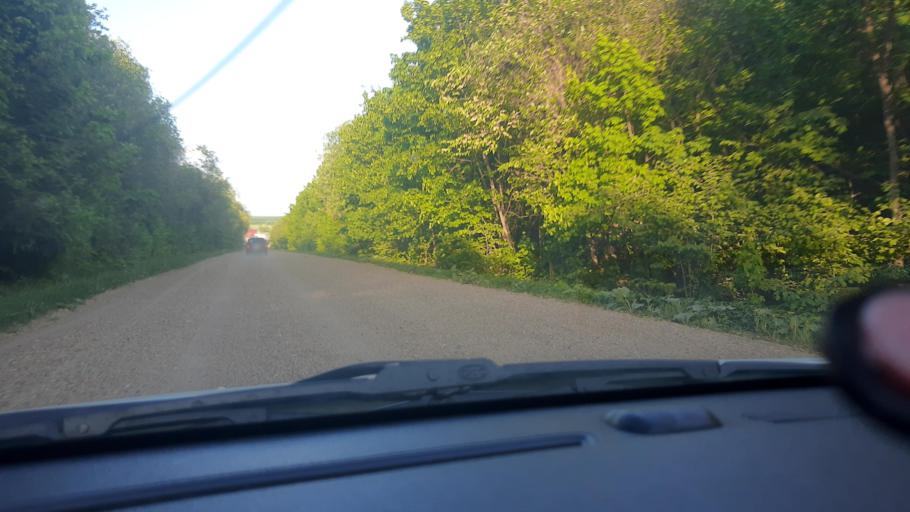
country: RU
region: Bashkortostan
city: Karmaskaly
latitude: 54.3802
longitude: 55.9306
